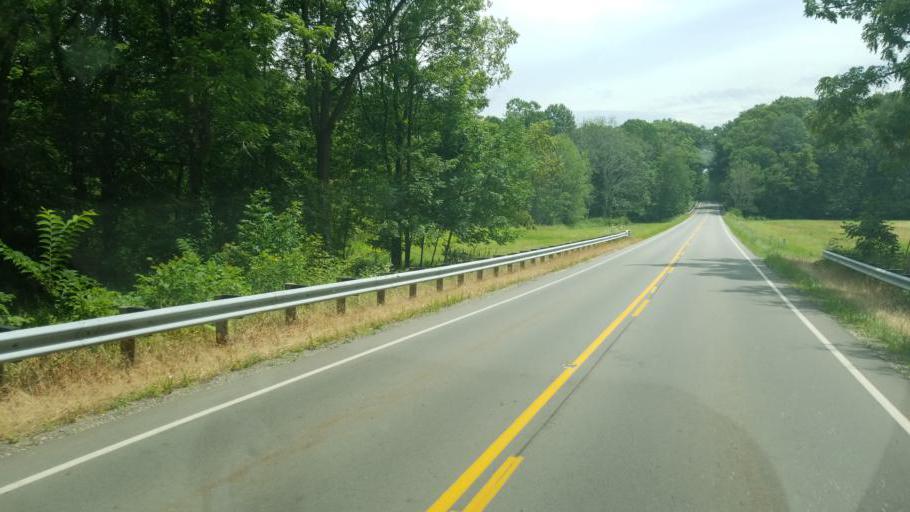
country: US
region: Ohio
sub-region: Richland County
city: Lexington
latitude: 40.7011
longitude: -82.6313
